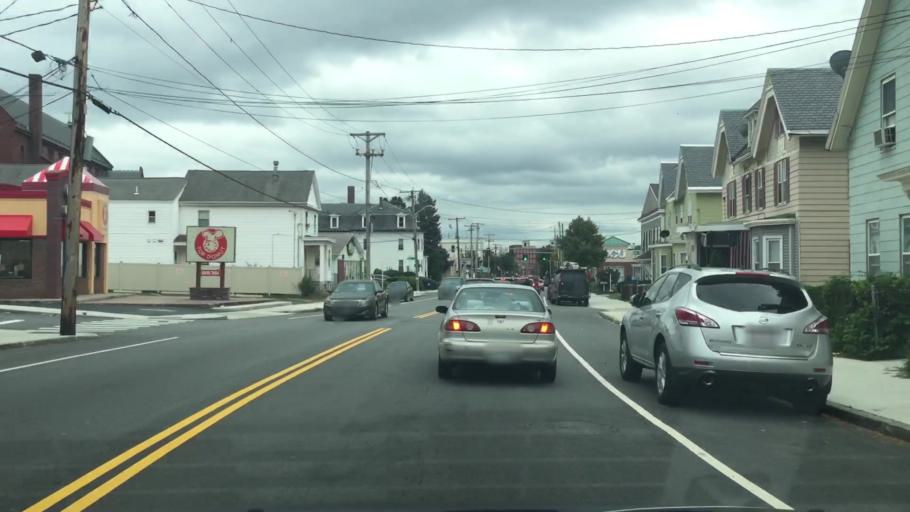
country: US
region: Massachusetts
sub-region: Middlesex County
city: Dracut
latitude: 42.6534
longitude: -71.3024
